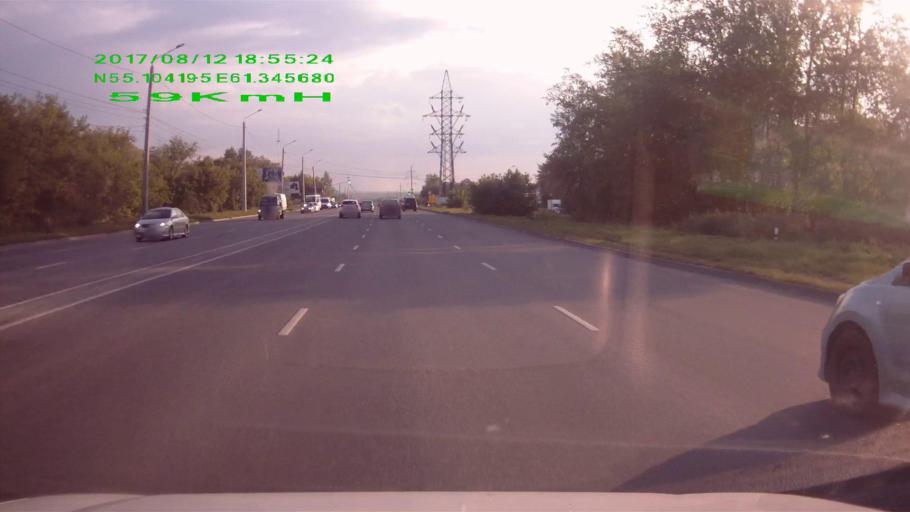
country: RU
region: Chelyabinsk
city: Novosineglazovskiy
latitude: 55.0984
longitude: 61.3375
